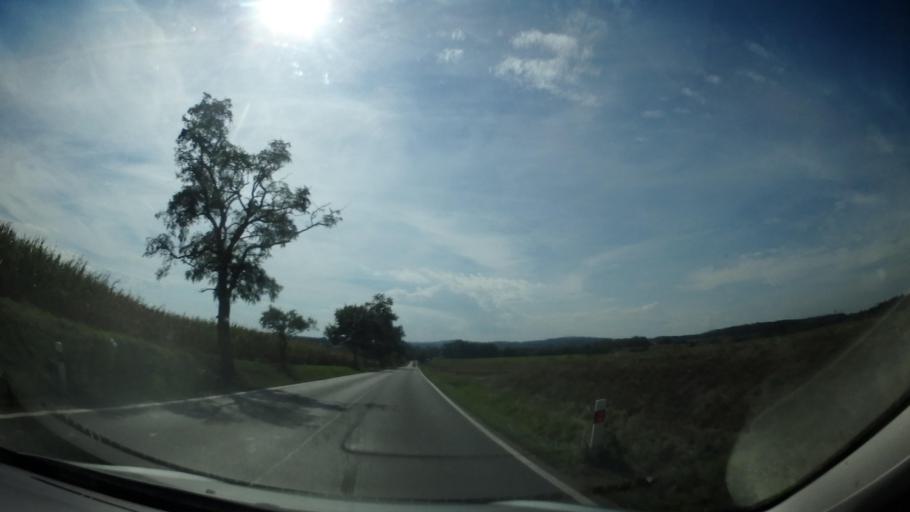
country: CZ
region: Jihocesky
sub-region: Okres Pisek
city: Pisek
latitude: 49.2999
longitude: 14.0625
